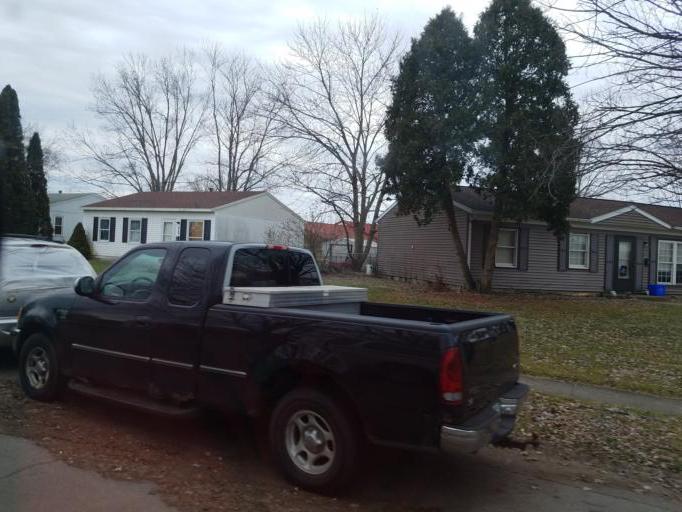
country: US
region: Ohio
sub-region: Marion County
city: Marion
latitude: 40.6087
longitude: -83.1154
